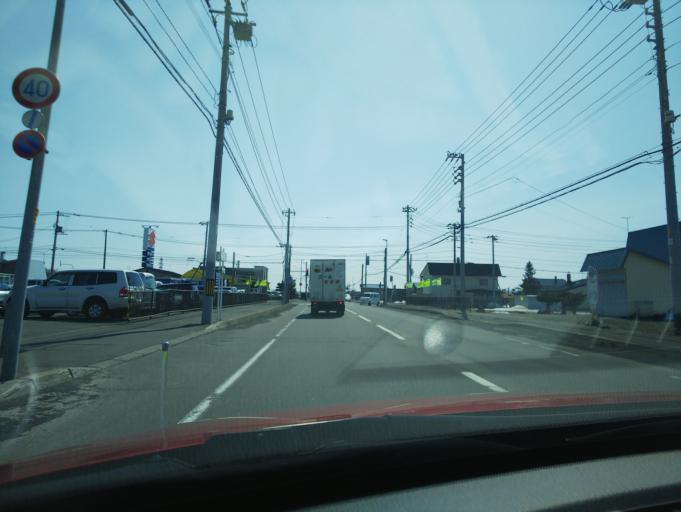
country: JP
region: Hokkaido
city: Nayoro
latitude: 44.3370
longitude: 142.4643
